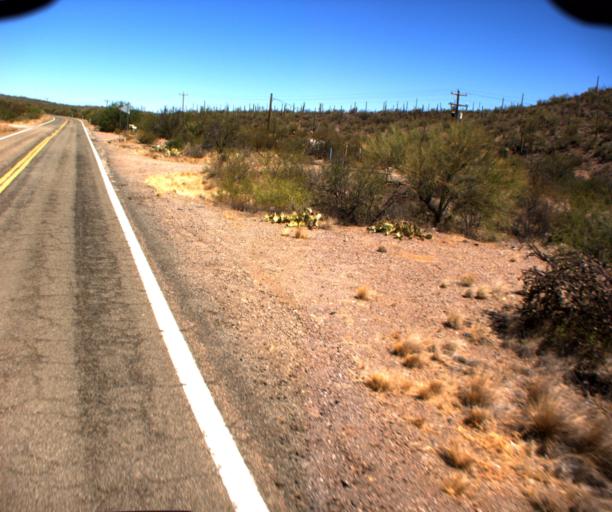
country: US
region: Arizona
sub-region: Pima County
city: Sells
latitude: 32.1728
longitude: -112.1533
